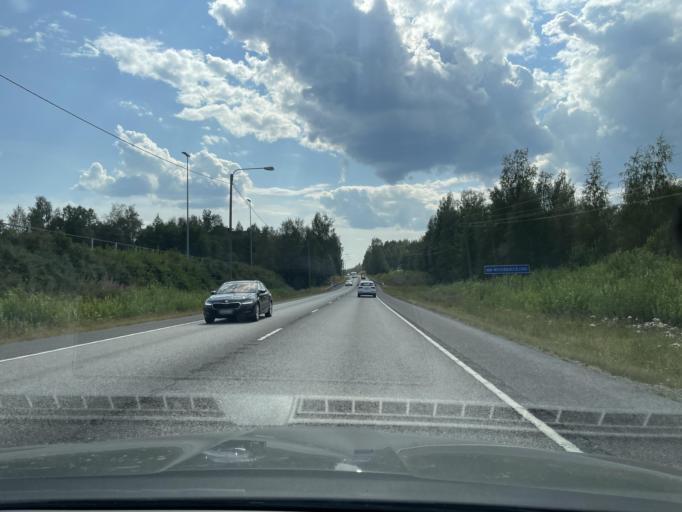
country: FI
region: Central Finland
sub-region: Jyvaeskylae
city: Muurame
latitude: 62.1314
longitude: 25.6664
